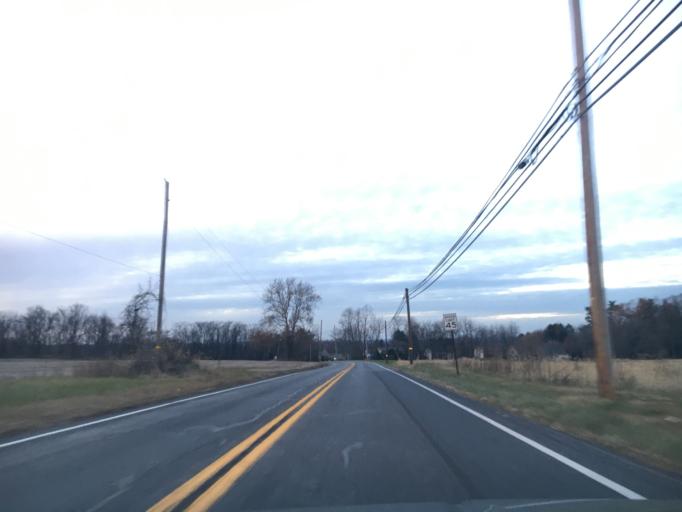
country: US
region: Pennsylvania
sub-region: Lehigh County
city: Stiles
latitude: 40.6418
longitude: -75.5156
